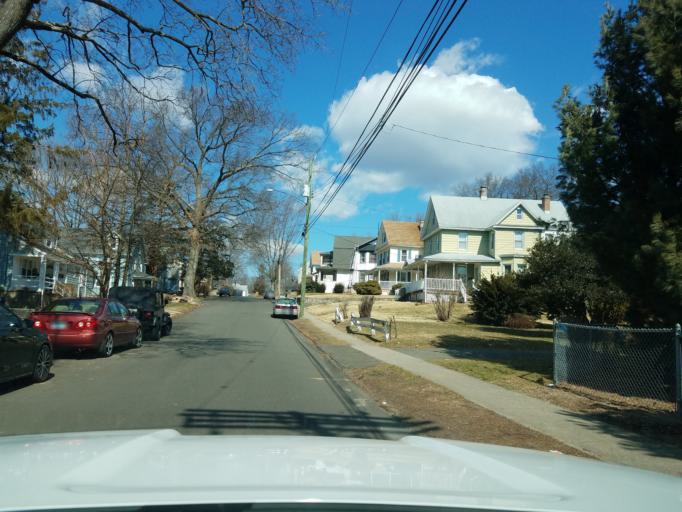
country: US
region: Connecticut
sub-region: Fairfield County
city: Stratford
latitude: 41.1993
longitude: -73.1345
